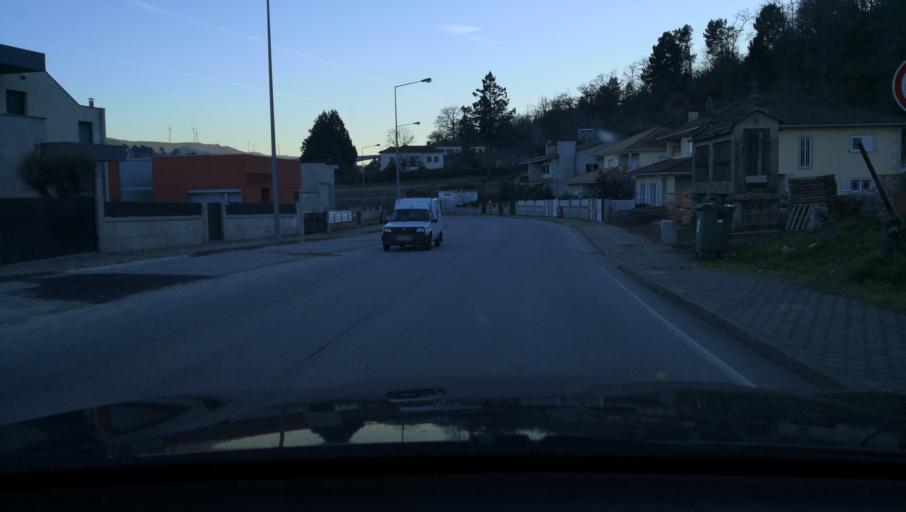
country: PT
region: Vila Real
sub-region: Vila Pouca de Aguiar
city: Vila Pouca de Aguiar
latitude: 41.4923
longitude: -7.6499
